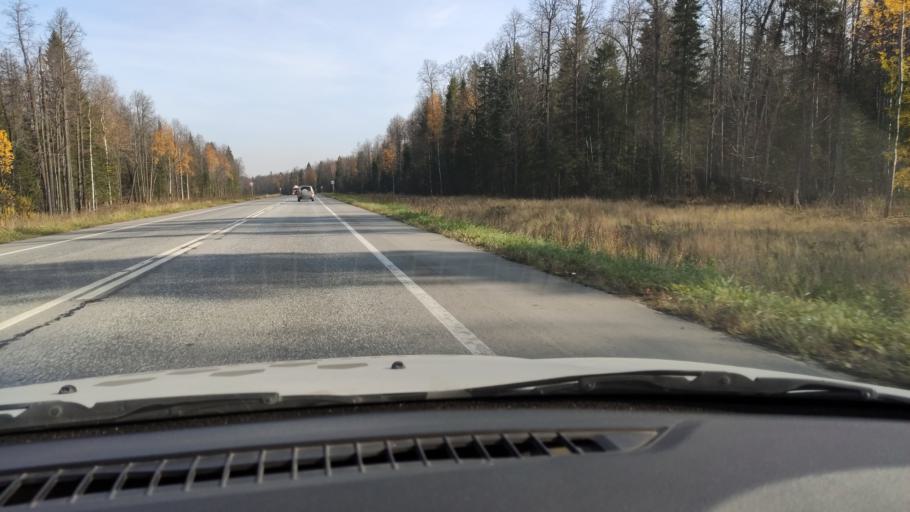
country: RU
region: Perm
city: Novyye Lyady
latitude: 58.0297
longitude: 56.5205
